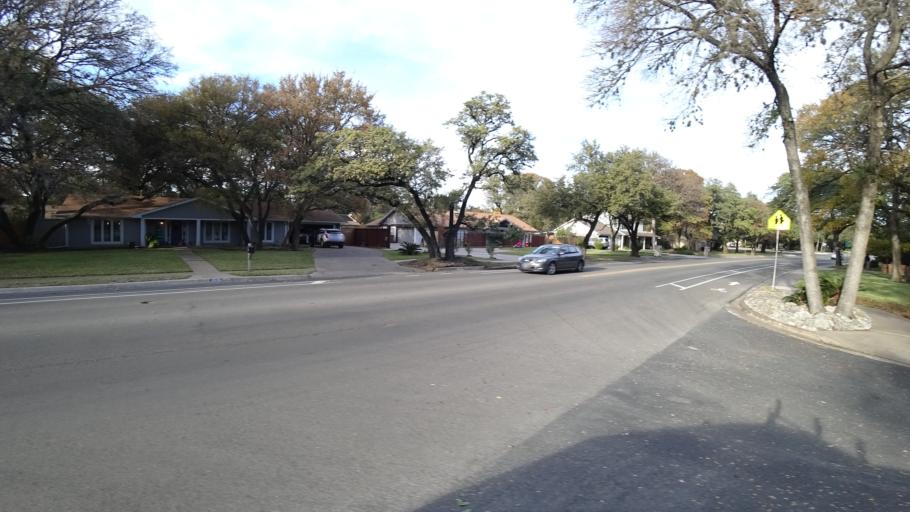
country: US
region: Texas
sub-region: Williamson County
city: Jollyville
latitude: 30.3796
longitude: -97.7520
